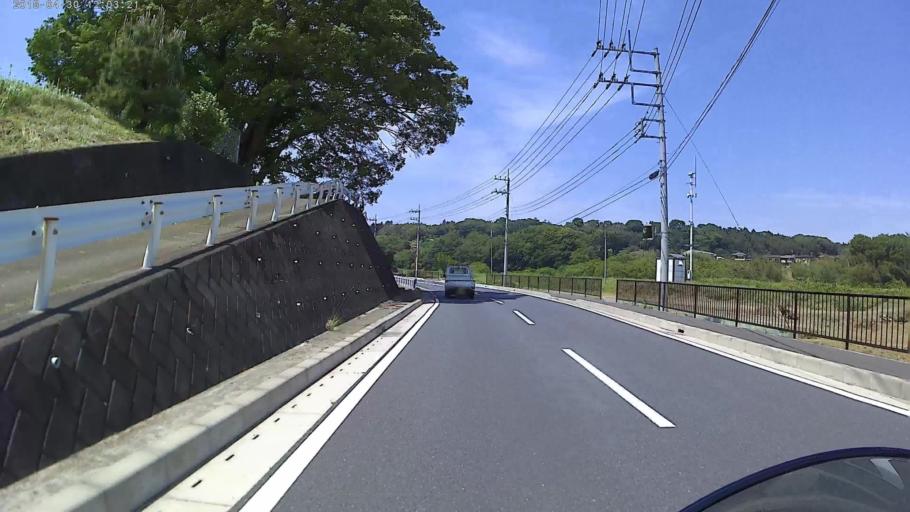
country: JP
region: Kanagawa
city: Zama
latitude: 35.5250
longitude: 139.3105
